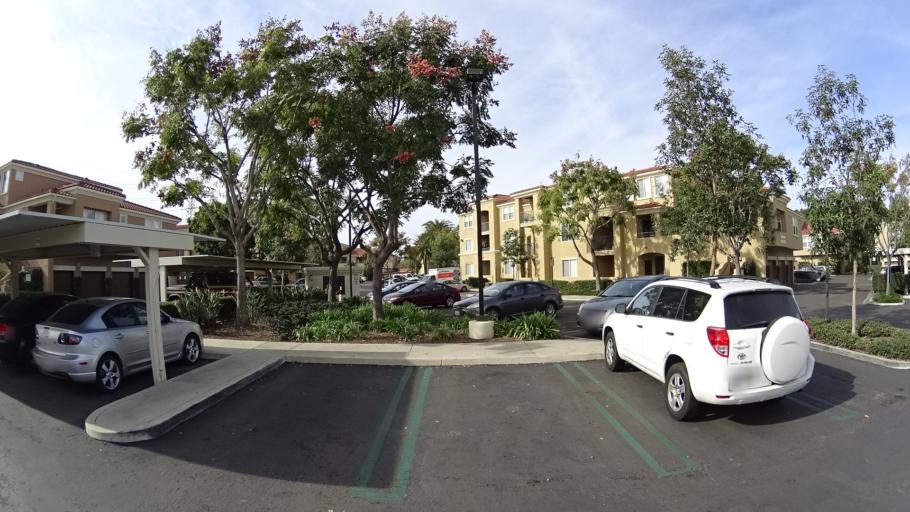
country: US
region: California
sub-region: Orange County
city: Laguna Woods
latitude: 33.5949
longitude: -117.7329
